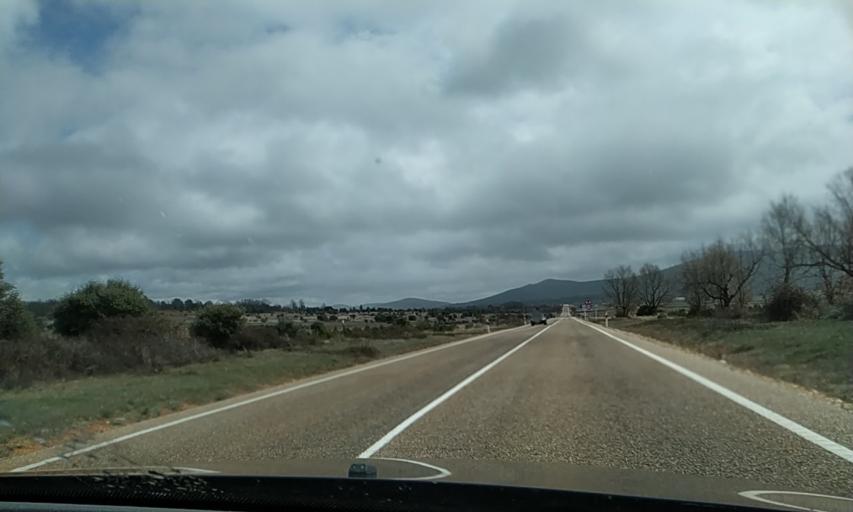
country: ES
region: Castille and Leon
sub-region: Provincia de Zamora
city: Ferreras de Abajo
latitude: 41.9138
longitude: -6.0835
